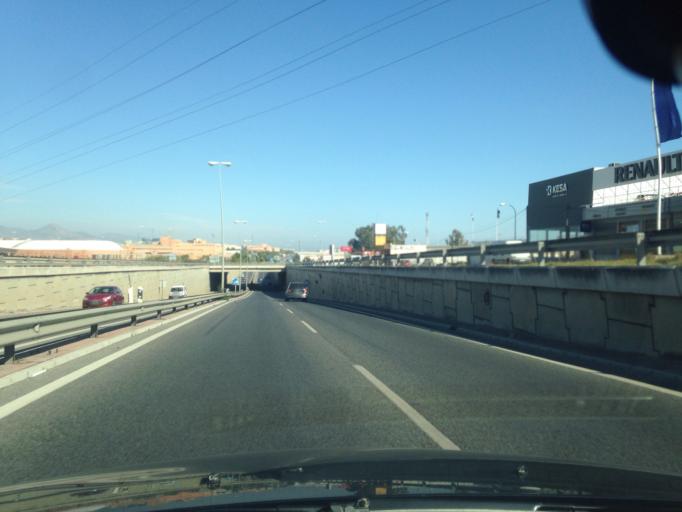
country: ES
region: Andalusia
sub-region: Provincia de Malaga
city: Malaga
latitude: 36.7140
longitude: -4.4857
